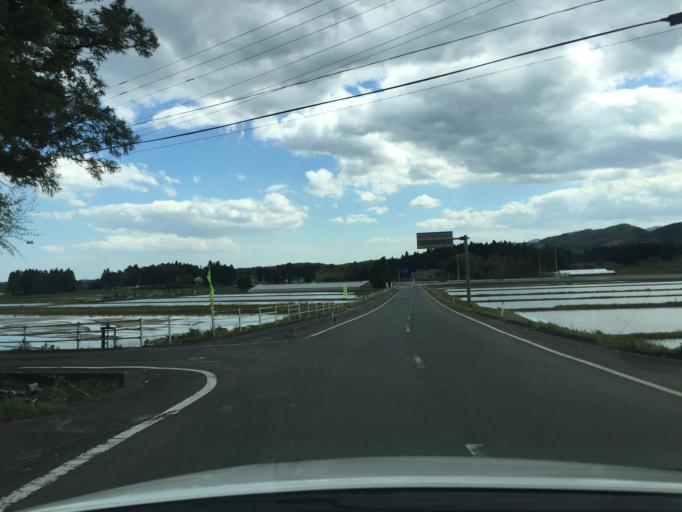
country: JP
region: Miyagi
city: Marumori
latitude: 37.7362
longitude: 140.9279
